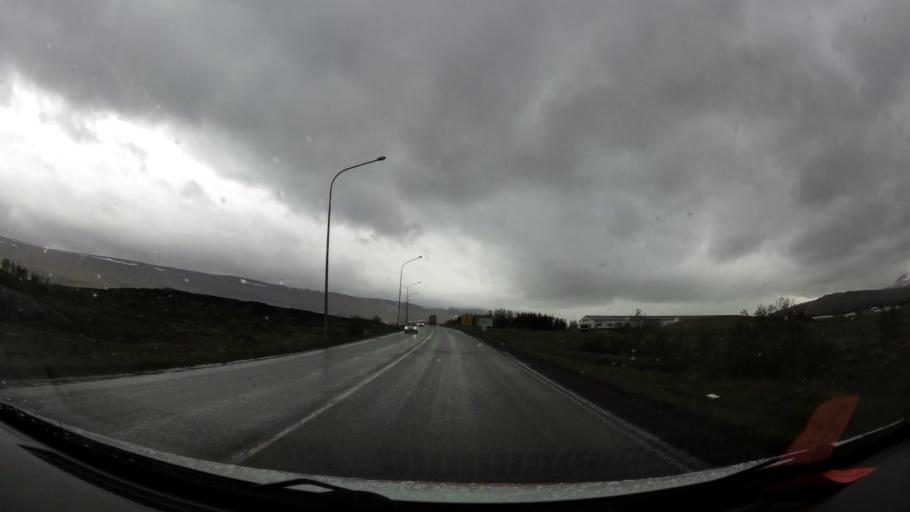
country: IS
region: Northeast
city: Akureyri
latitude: 65.7015
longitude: -18.1479
